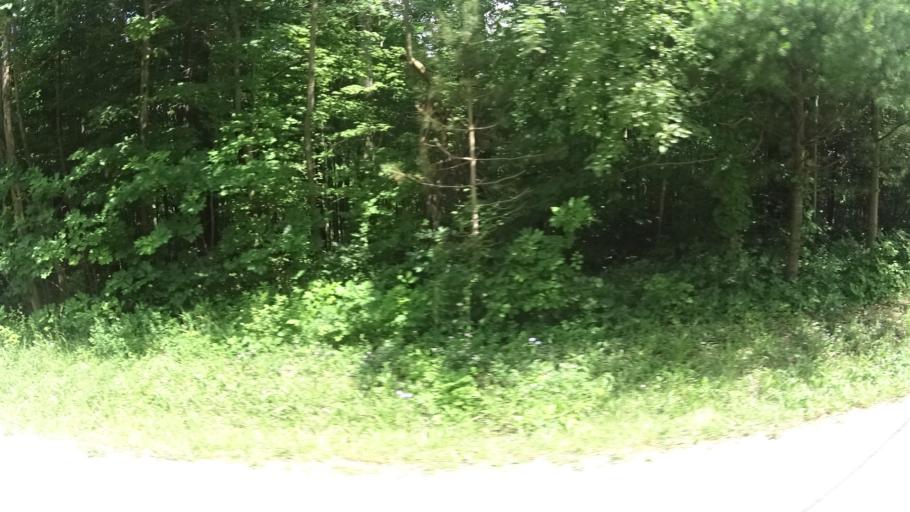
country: US
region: Ohio
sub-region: Huron County
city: Wakeman
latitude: 41.3198
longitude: -82.3705
